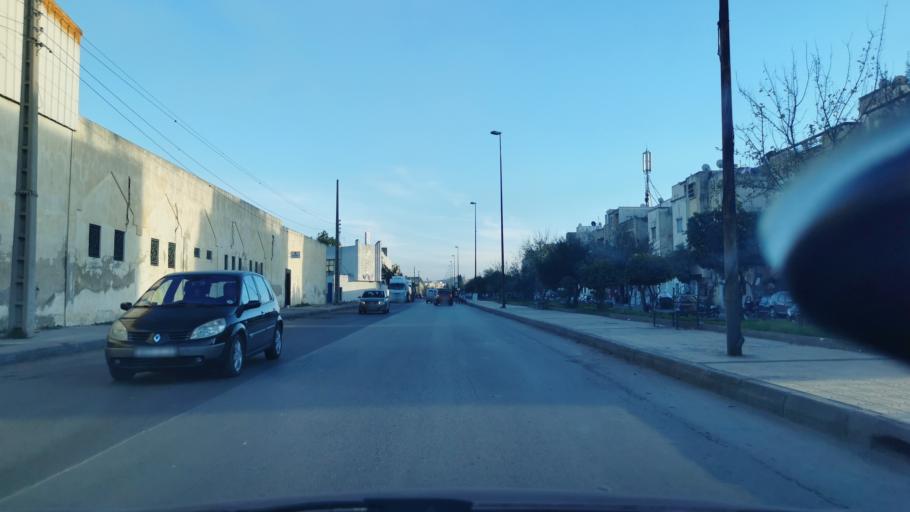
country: MA
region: Fes-Boulemane
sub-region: Fes
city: Fes
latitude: 34.0260
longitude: -4.9861
